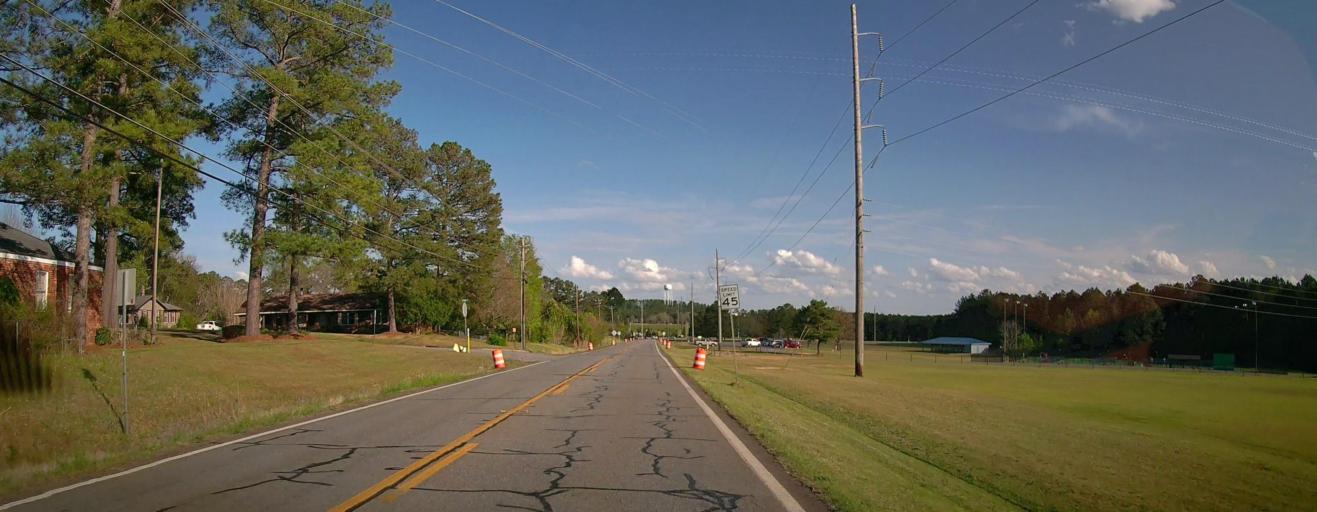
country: US
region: Georgia
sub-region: Baldwin County
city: Milledgeville
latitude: 33.0992
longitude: -83.2701
